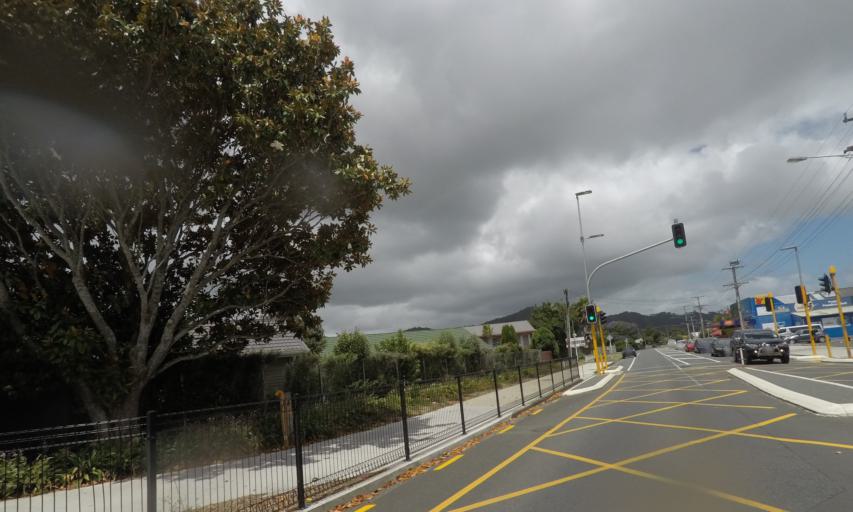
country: NZ
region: Northland
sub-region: Whangarei
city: Whangarei
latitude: -35.7039
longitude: 174.3173
